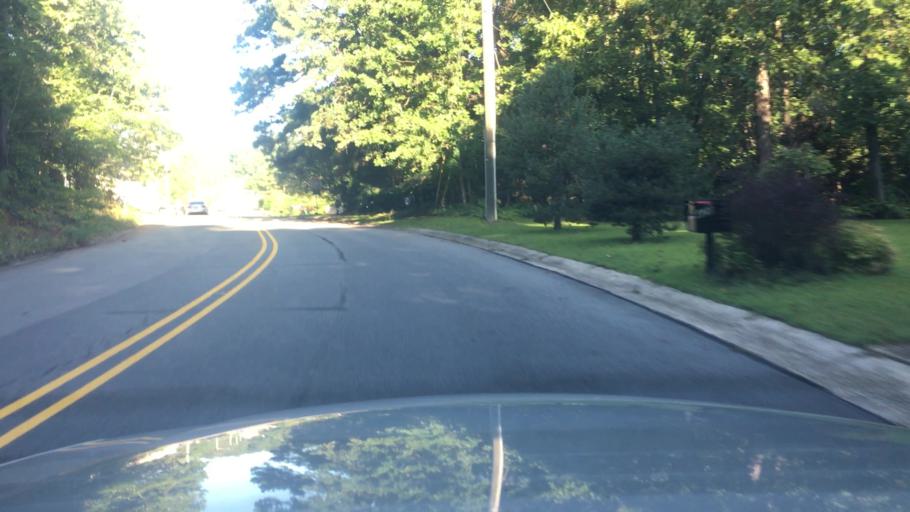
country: US
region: North Carolina
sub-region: Cumberland County
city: Fayetteville
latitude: 35.1196
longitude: -78.8728
